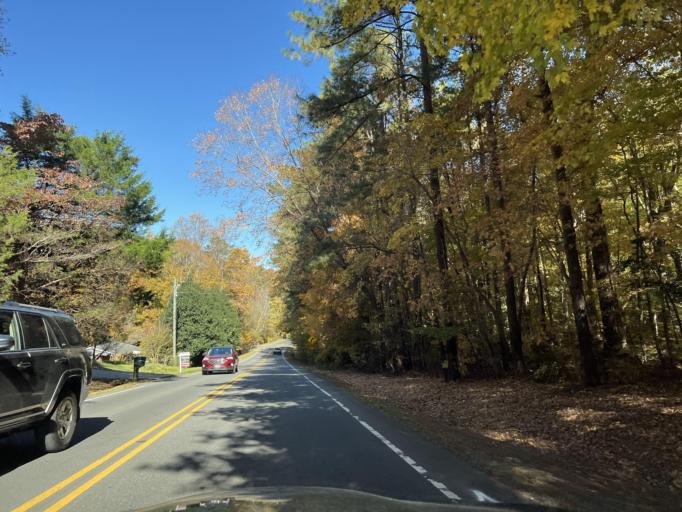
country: US
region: North Carolina
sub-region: Wake County
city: Fuquay-Varina
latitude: 35.6326
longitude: -78.7291
